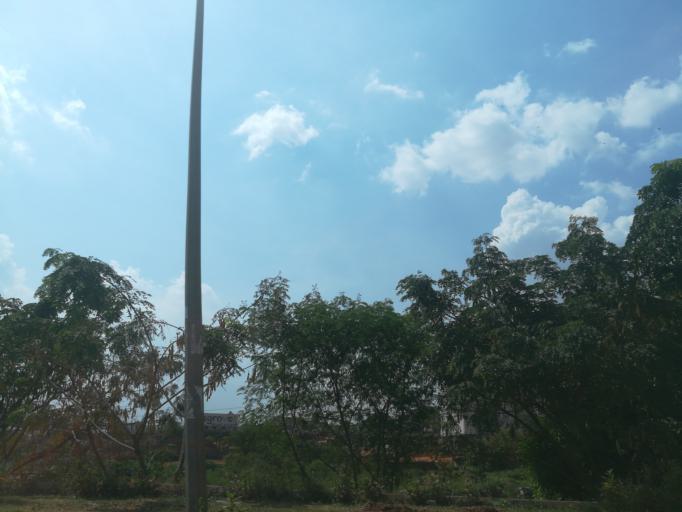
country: NG
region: Abuja Federal Capital Territory
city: Abuja
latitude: 9.0578
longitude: 7.4534
